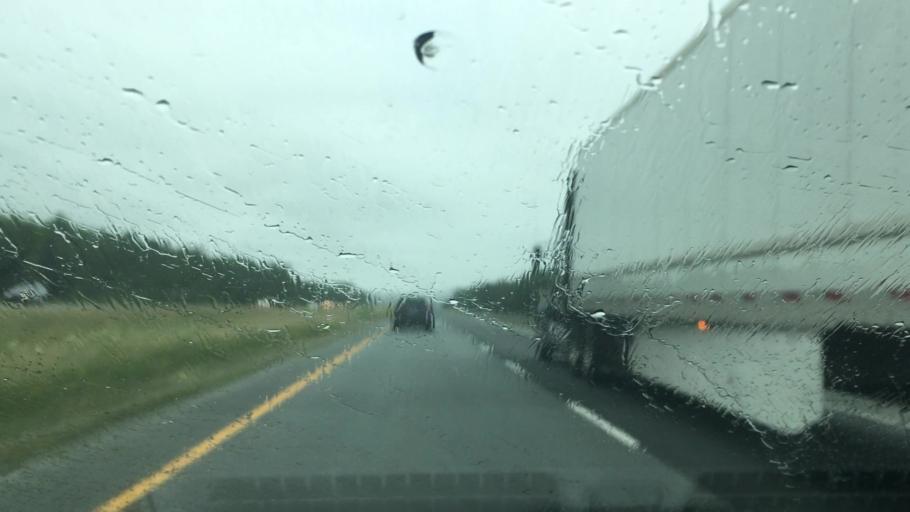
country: CA
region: Nova Scotia
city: Truro
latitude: 45.2348
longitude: -63.2947
